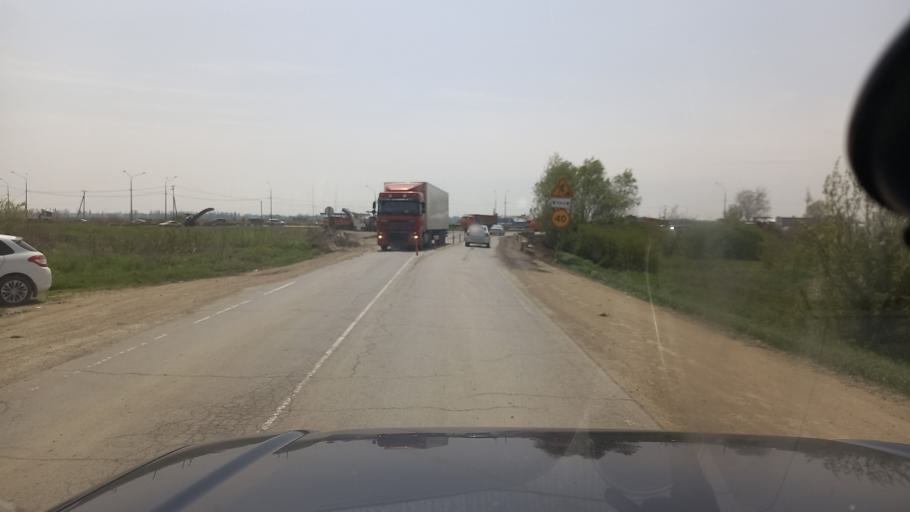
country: RU
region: Adygeya
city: Takhtamukay
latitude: 44.9537
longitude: 38.9977
